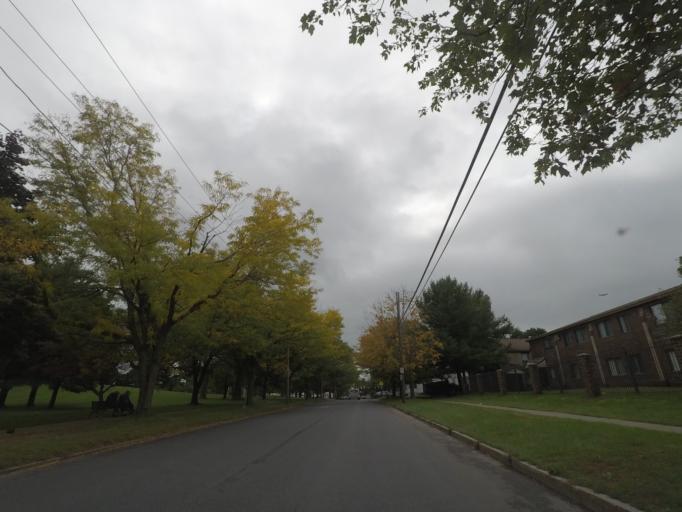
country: US
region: New York
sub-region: Albany County
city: West Albany
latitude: 42.6725
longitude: -73.7780
